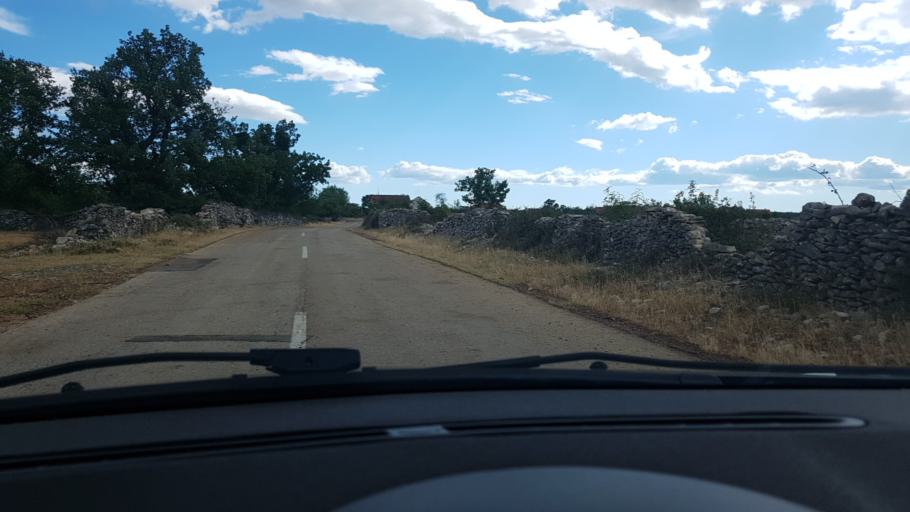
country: HR
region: Sibensko-Kniniska
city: Kistanje
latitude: 44.0589
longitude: 15.9284
